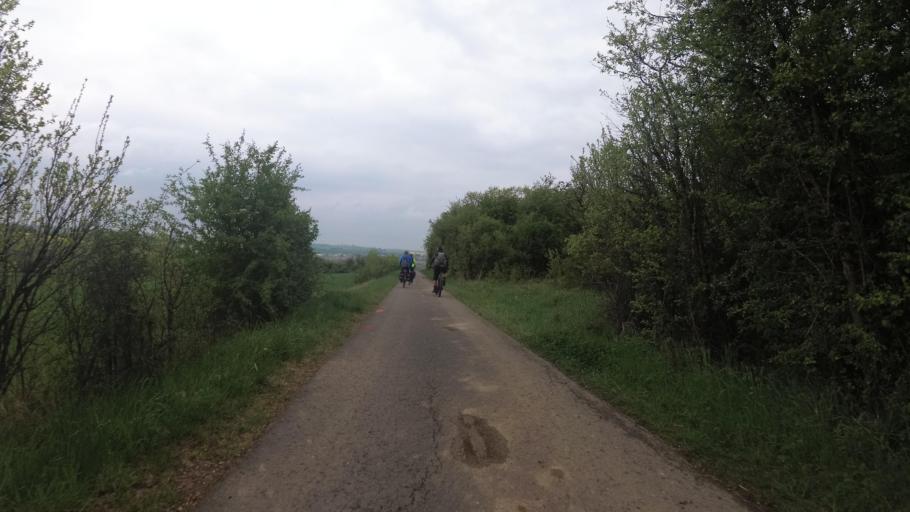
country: DE
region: Saarland
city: Rehlingen-Siersburg
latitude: 49.3115
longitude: 6.6542
